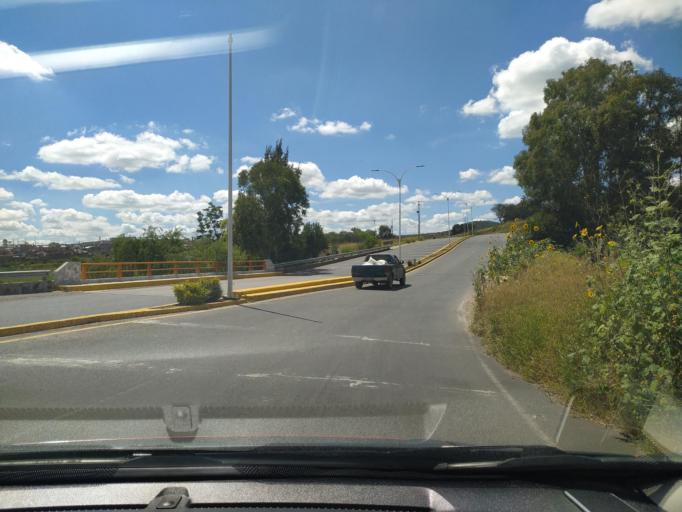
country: MX
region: Jalisco
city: San Miguel el Alto
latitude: 21.0372
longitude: -102.4099
